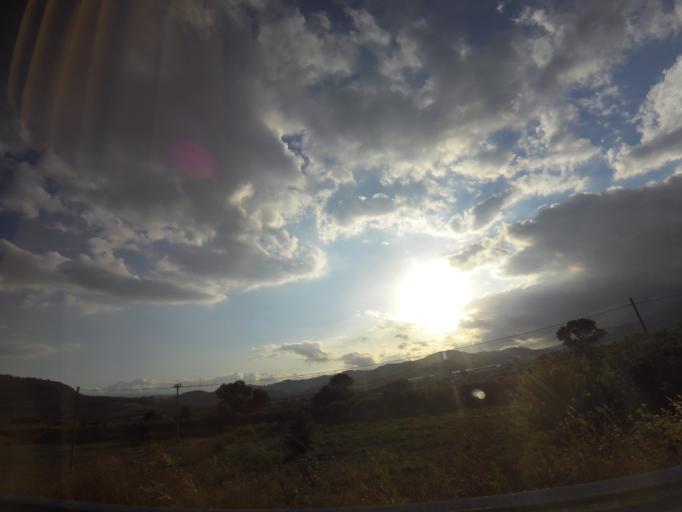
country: IT
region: Calabria
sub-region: Provincia di Catanzaro
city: Catanzaro
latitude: 38.8850
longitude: 16.5556
